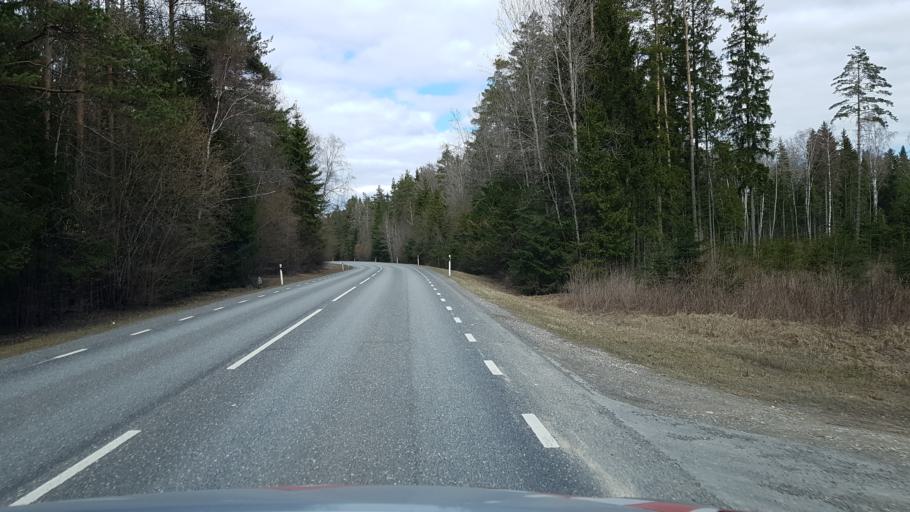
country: EE
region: Laeaene-Virumaa
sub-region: Vaeike-Maarja vald
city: Vaike-Maarja
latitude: 59.0724
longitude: 26.2390
